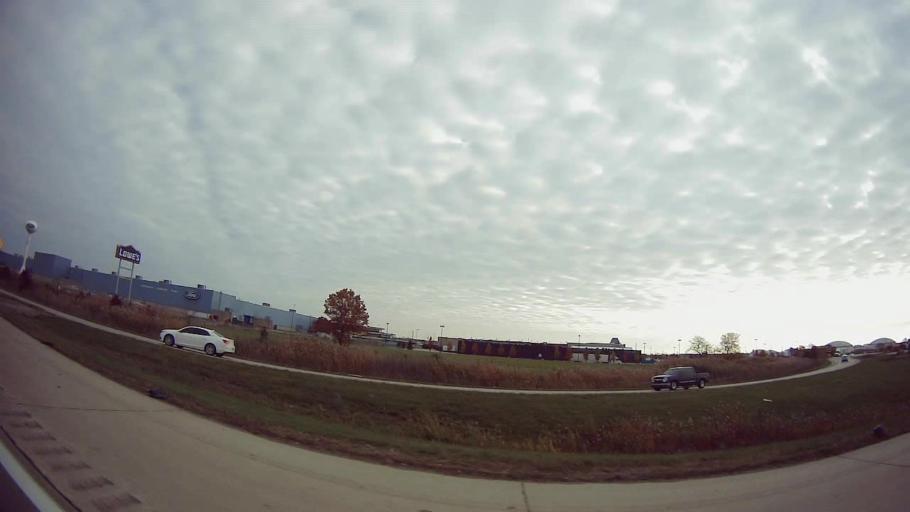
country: US
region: Michigan
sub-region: Wayne County
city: Woodhaven
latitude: 42.1417
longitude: -83.2415
